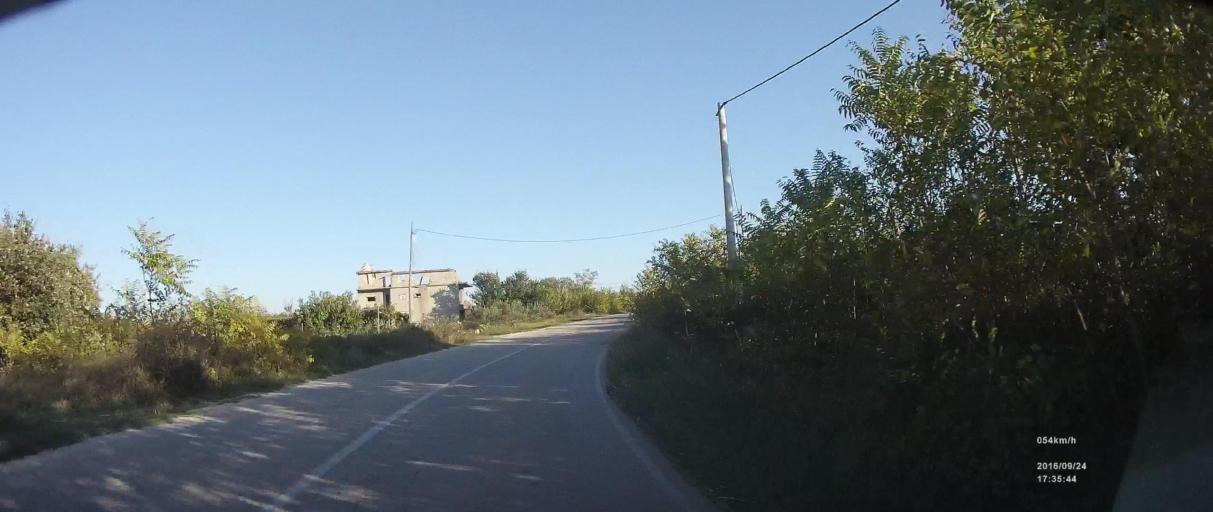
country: HR
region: Zadarska
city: Posedarje
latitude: 44.1591
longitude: 15.4694
